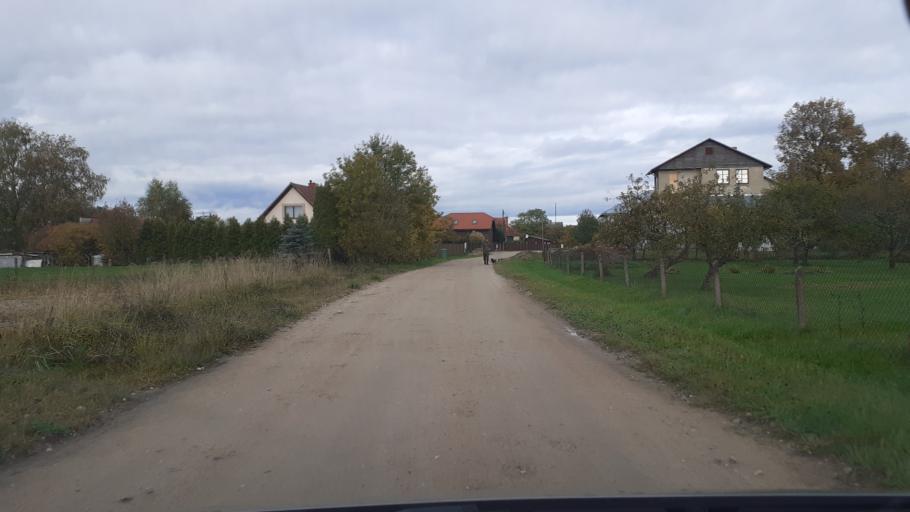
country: LV
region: Kuldigas Rajons
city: Kuldiga
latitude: 56.9648
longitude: 21.9937
